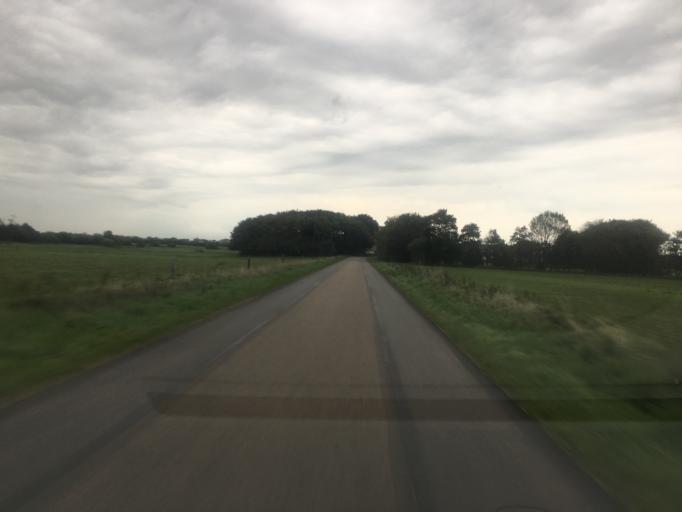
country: DK
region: South Denmark
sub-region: Tonder Kommune
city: Logumkloster
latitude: 54.9975
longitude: 9.0150
